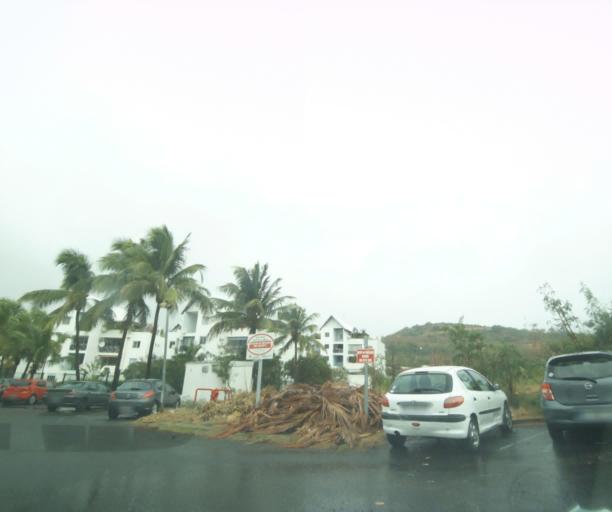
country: RE
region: Reunion
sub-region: Reunion
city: Saint-Paul
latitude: -21.0321
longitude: 55.2290
